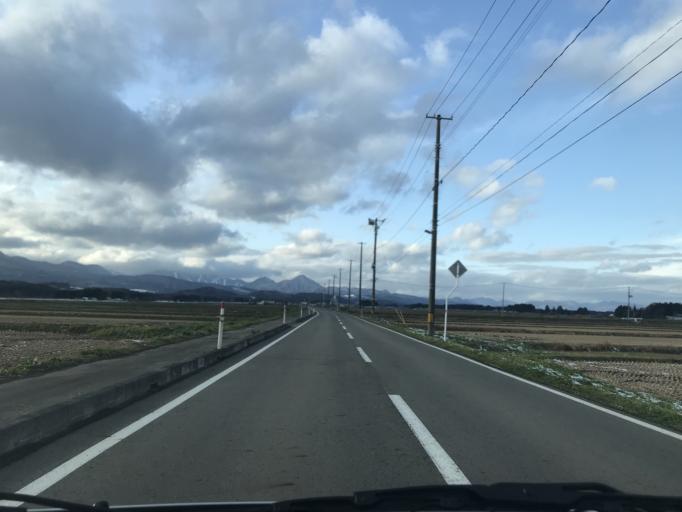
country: JP
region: Iwate
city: Mizusawa
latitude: 39.1985
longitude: 141.0652
